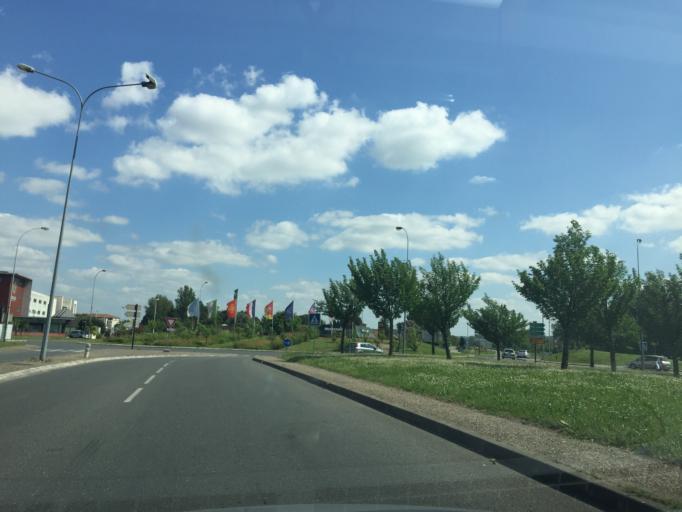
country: FR
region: Aquitaine
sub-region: Departement du Lot-et-Garonne
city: Le Passage
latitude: 44.1912
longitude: 0.6129
